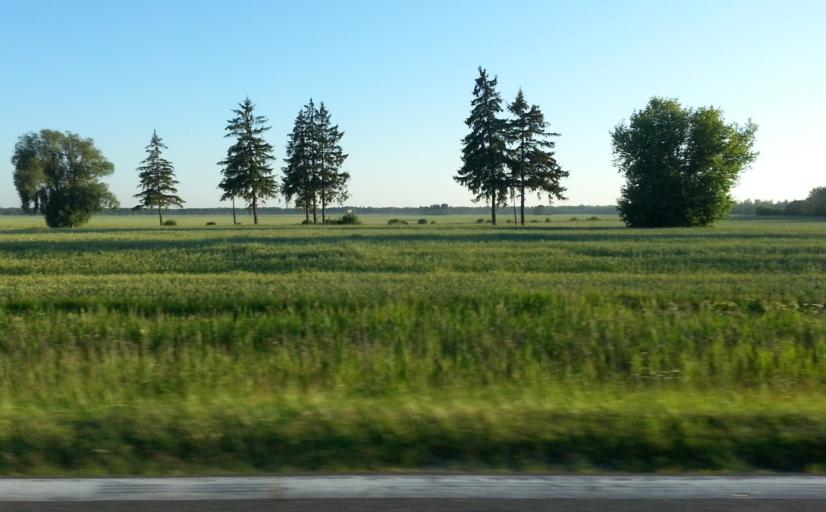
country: LT
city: Ramygala
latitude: 55.5389
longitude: 24.5387
